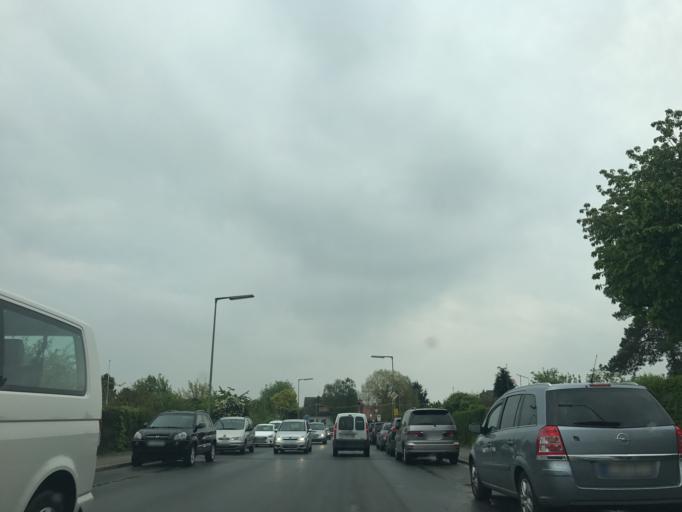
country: DE
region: Berlin
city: Staaken
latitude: 52.5393
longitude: 13.1552
